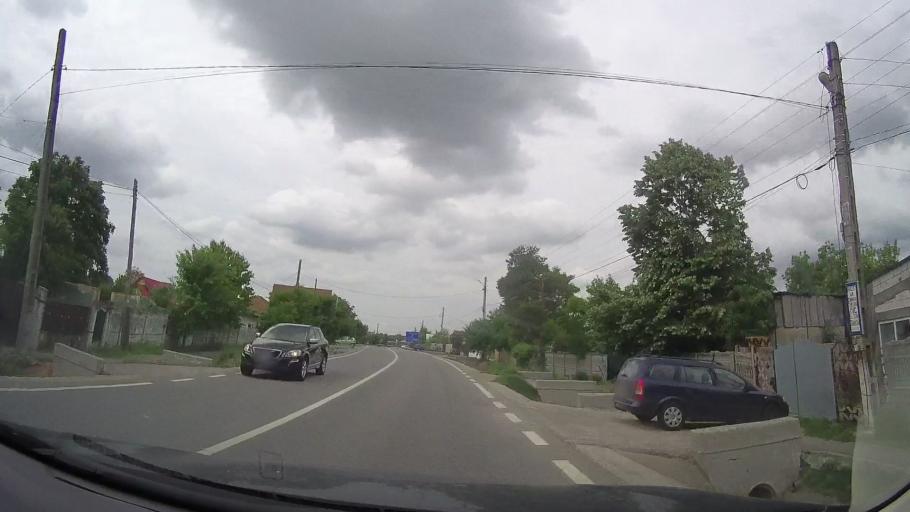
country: RO
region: Dolj
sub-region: Comuna Leu
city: Leu
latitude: 44.1873
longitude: 24.0077
